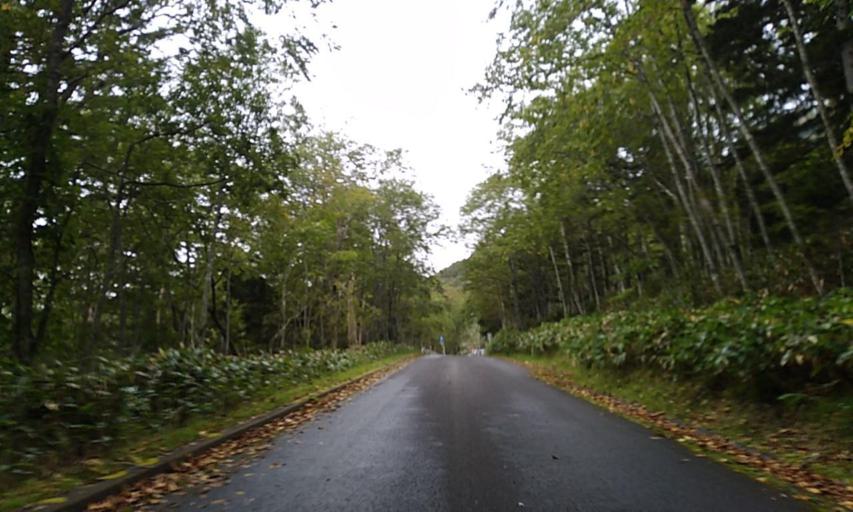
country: JP
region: Hokkaido
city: Bihoro
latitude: 43.5815
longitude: 144.2335
